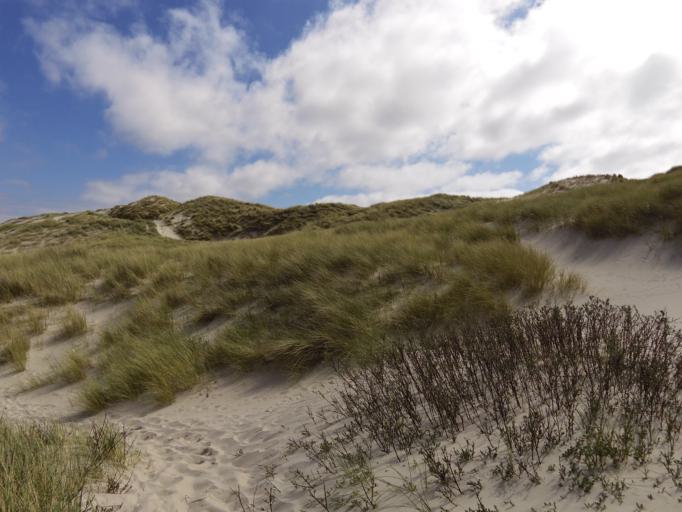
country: DE
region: Schleswig-Holstein
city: Nebel
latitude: 54.6234
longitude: 8.3599
